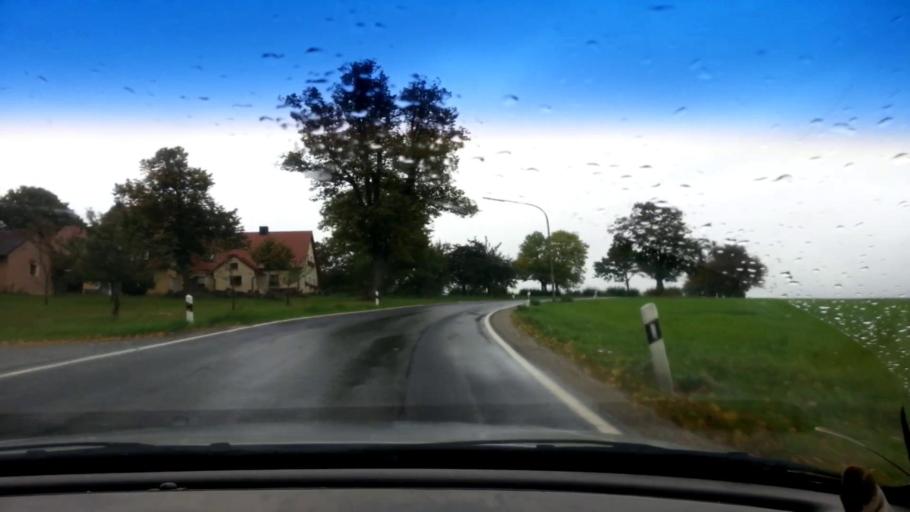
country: DE
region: Bavaria
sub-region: Upper Franconia
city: Poxdorf
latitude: 49.9399
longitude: 11.0790
